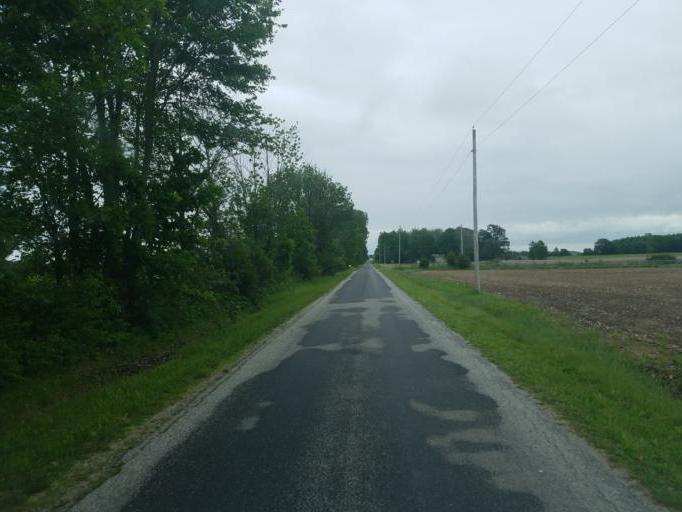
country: US
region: Ohio
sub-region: Marion County
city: Marion
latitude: 40.5055
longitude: -83.0429
